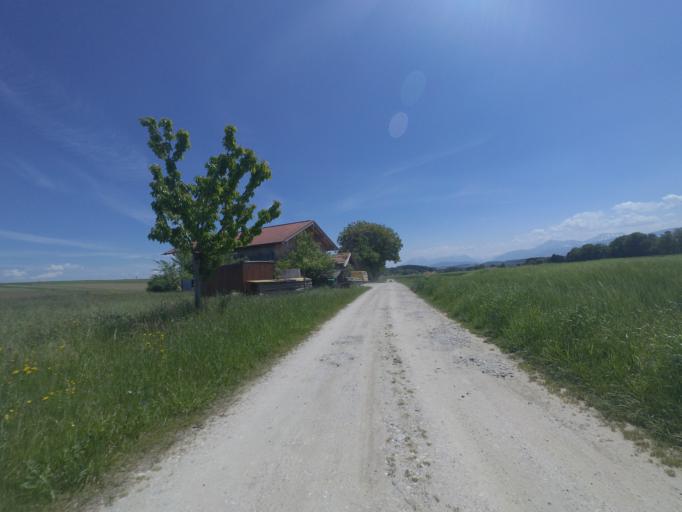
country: DE
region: Bavaria
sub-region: Upper Bavaria
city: Petting
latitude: 47.9397
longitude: 12.7977
